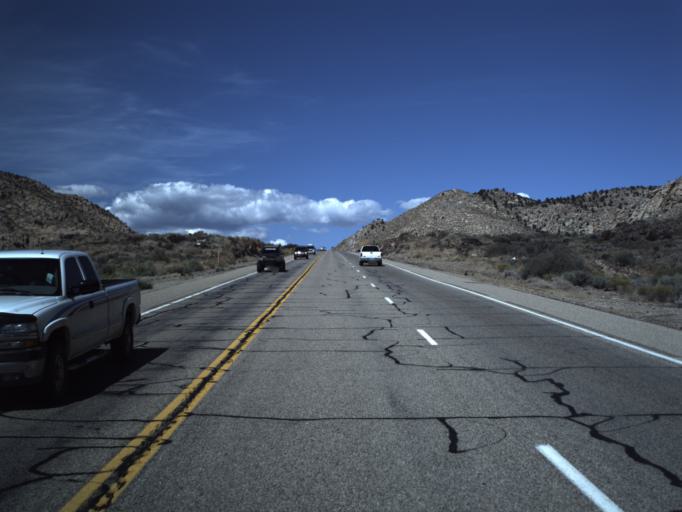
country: US
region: Utah
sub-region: Washington County
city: Ivins
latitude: 37.2357
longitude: -113.6353
